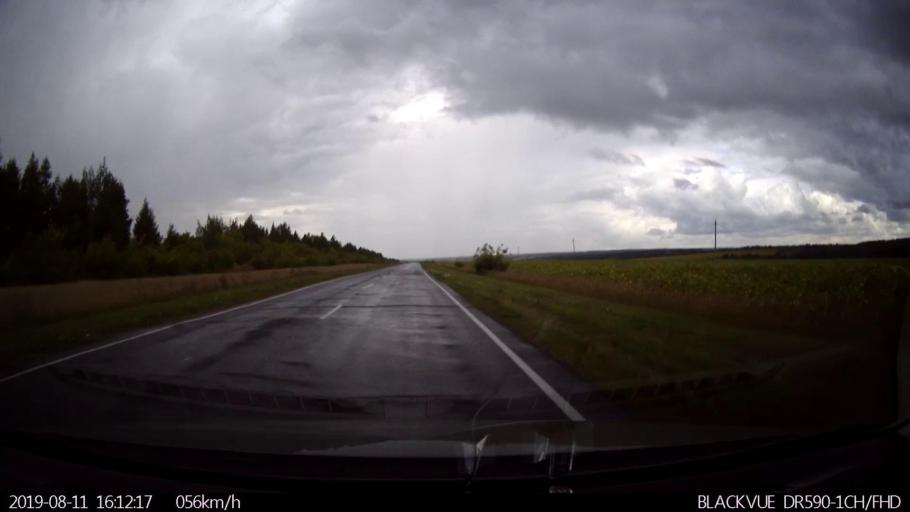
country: RU
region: Ulyanovsk
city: Ignatovka
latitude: 54.0102
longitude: 47.6409
